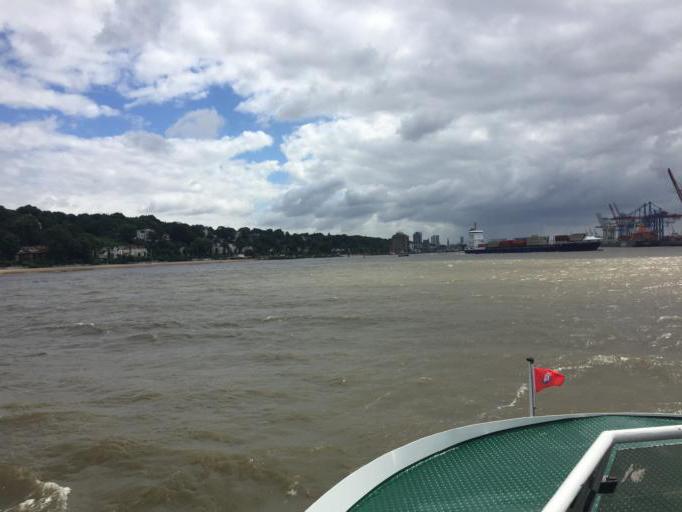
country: DE
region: Hamburg
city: Altona
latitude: 53.5415
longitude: 9.8956
